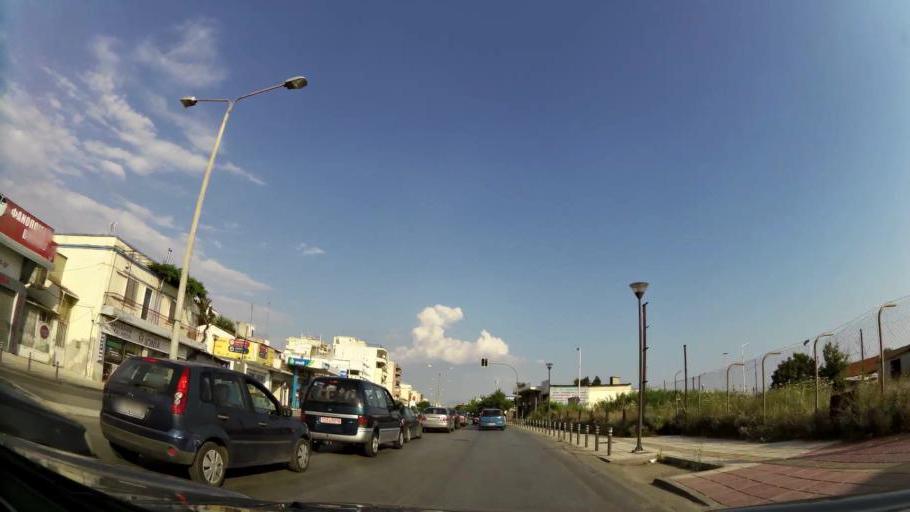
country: GR
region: Central Macedonia
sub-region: Nomos Thessalonikis
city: Menemeni
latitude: 40.6692
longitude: 22.8872
